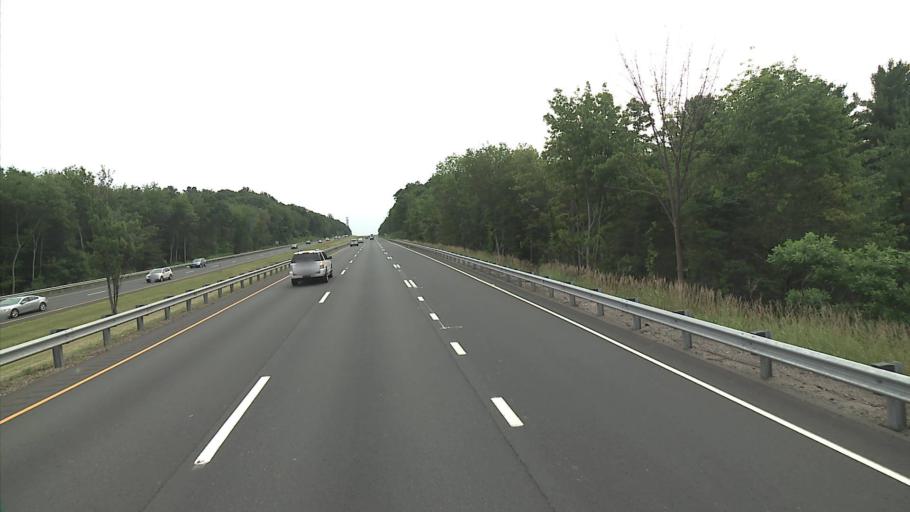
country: US
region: Connecticut
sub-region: New Haven County
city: Middlebury
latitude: 41.5097
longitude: -73.1353
